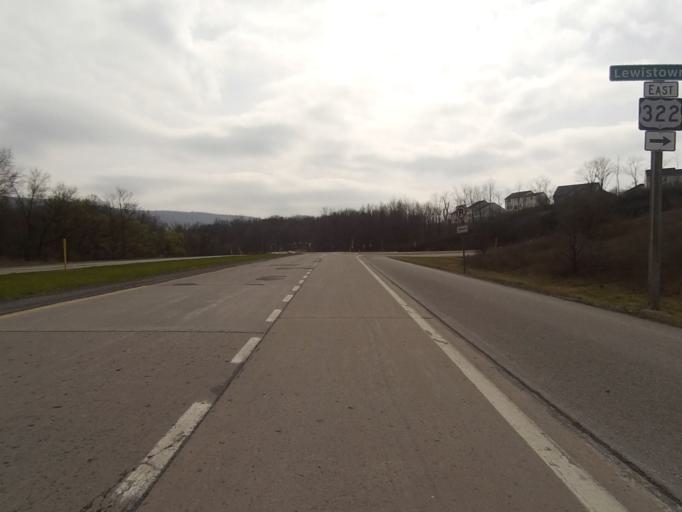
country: US
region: Pennsylvania
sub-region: Centre County
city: Boalsburg
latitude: 40.7888
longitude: -77.7996
